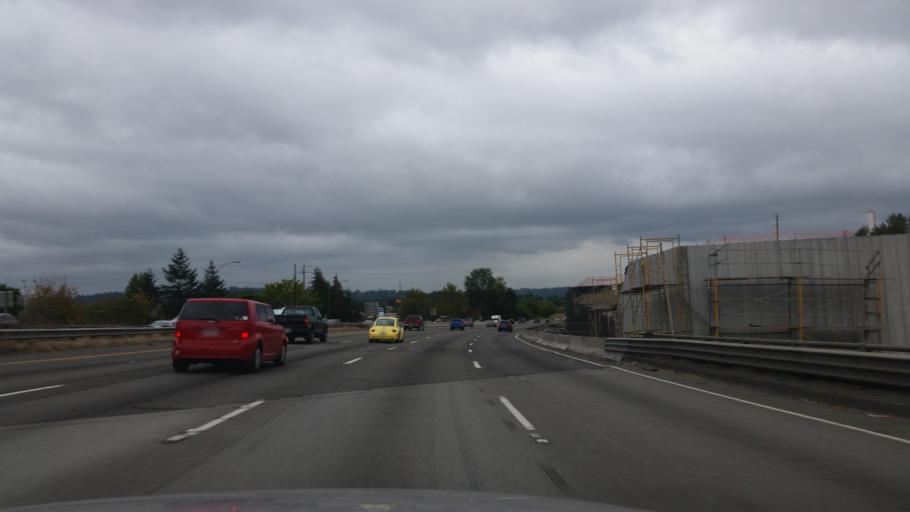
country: US
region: Washington
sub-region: Pierce County
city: Fife
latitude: 47.2416
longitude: -122.3974
